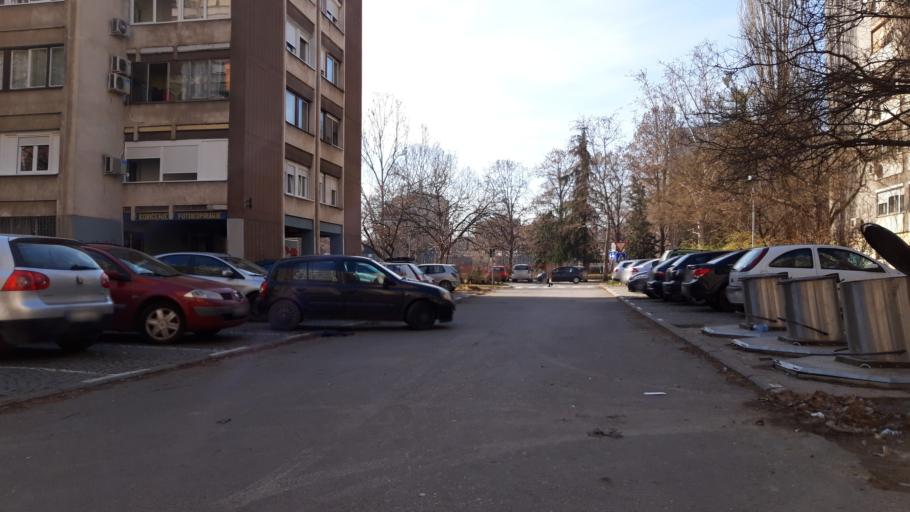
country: RS
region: Autonomna Pokrajina Vojvodina
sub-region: Juznobacki Okrug
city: Novi Sad
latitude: 45.2619
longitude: 19.8298
